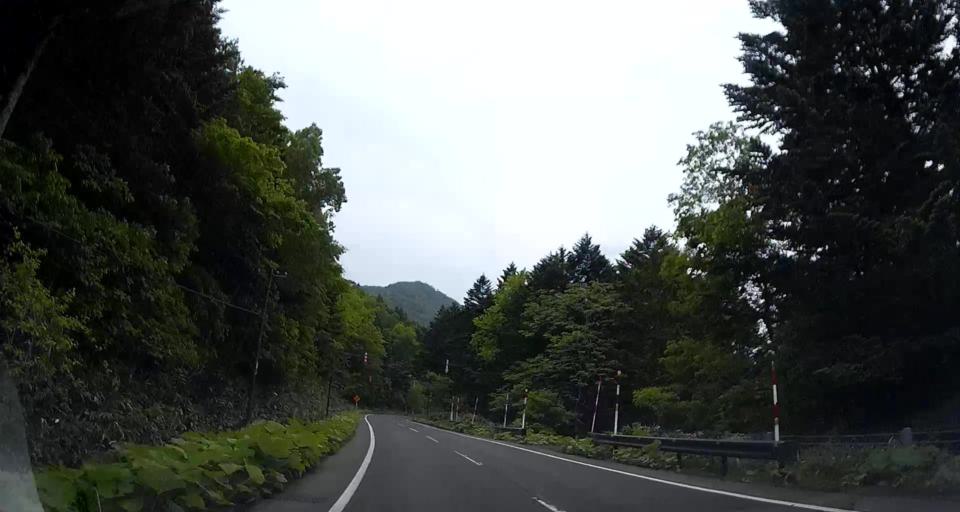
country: JP
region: Hokkaido
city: Shiraoi
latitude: 42.6498
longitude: 141.2040
